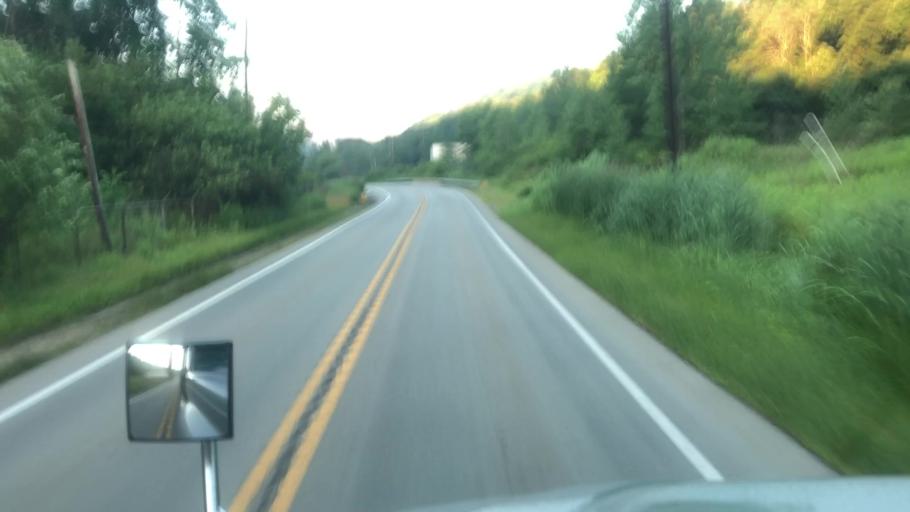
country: US
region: Pennsylvania
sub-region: Venango County
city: Hasson Heights
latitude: 41.4797
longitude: -79.6774
